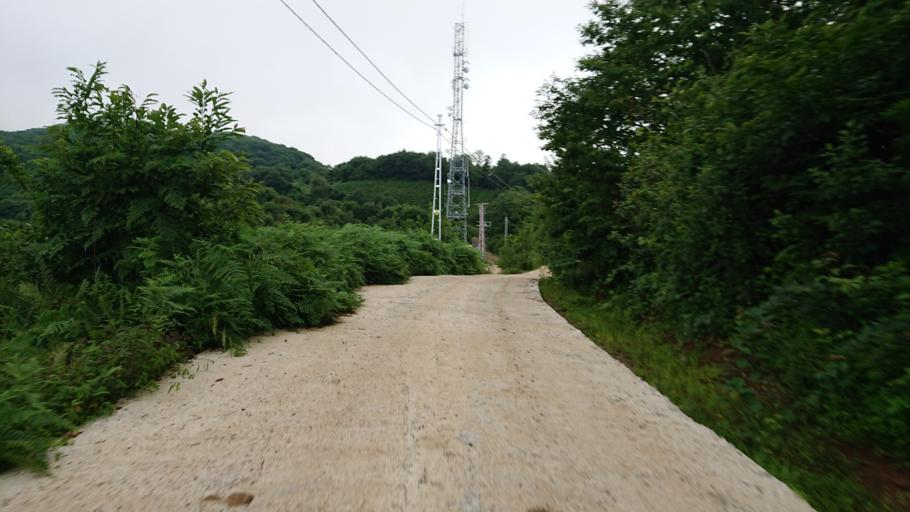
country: TR
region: Rize
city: Rize
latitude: 40.9903
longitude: 40.5095
